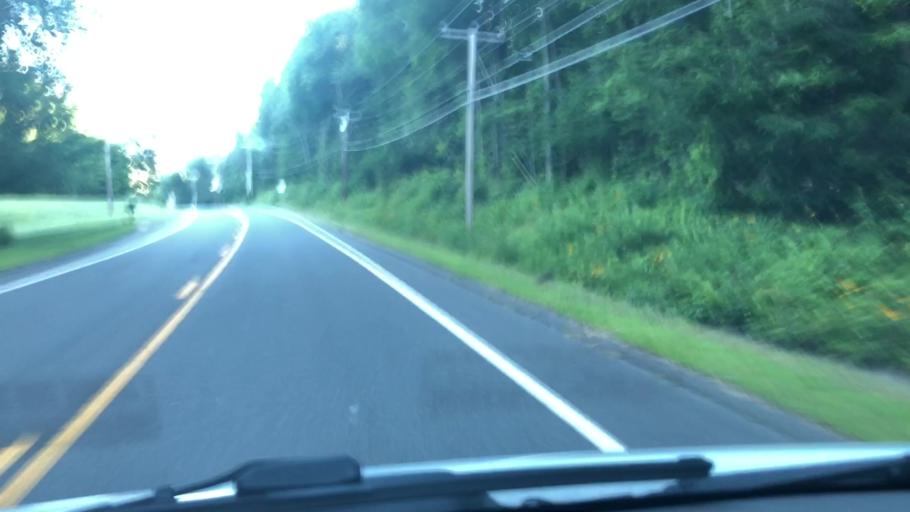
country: US
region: Massachusetts
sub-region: Hampshire County
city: Westhampton
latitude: 42.2869
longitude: -72.8018
